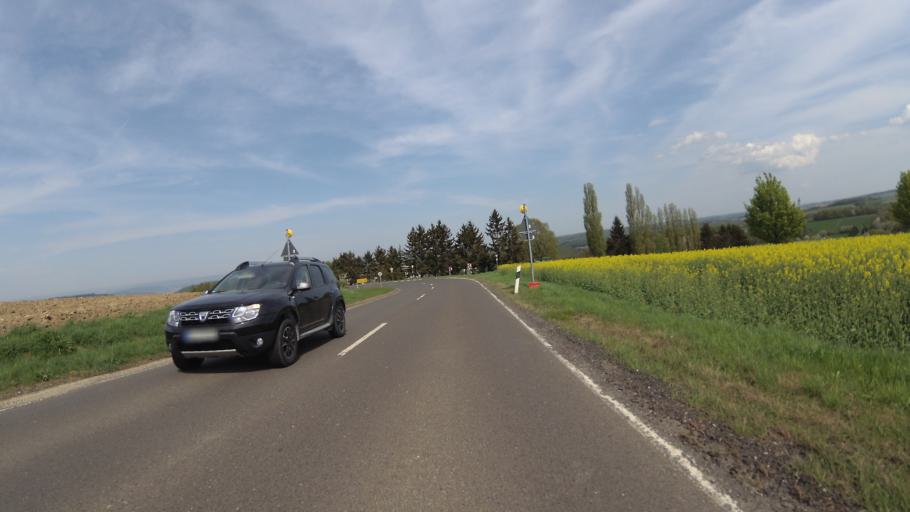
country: DE
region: Rheinland-Pfalz
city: Longkamp
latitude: 49.8808
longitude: 7.1235
